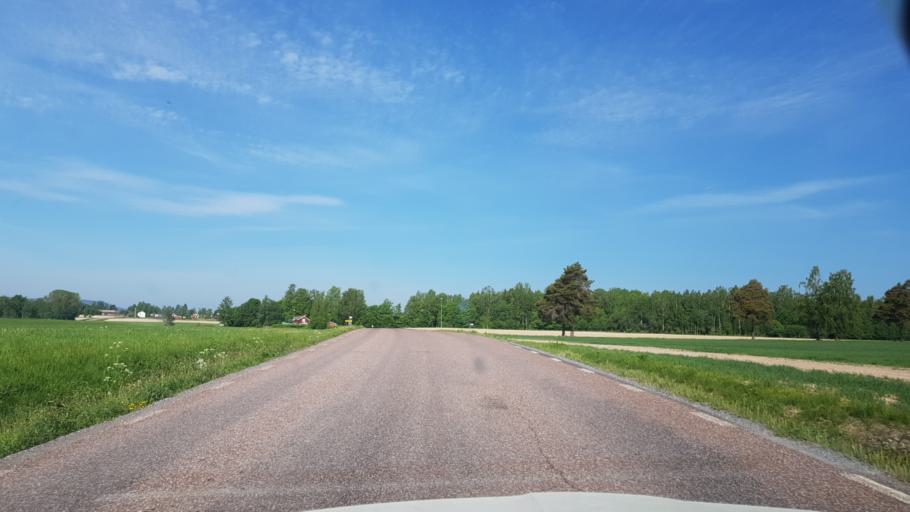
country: SE
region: Dalarna
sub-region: Borlange Kommun
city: Ornas
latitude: 60.4259
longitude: 15.6400
